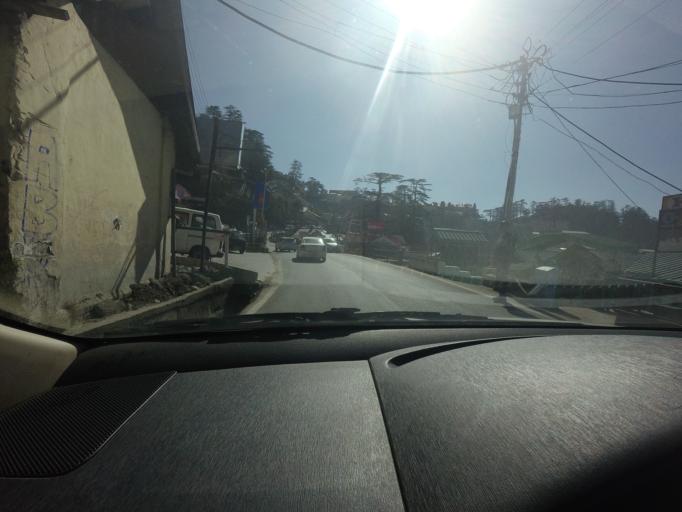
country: IN
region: Himachal Pradesh
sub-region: Shimla
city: Shimla
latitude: 31.1085
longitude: 77.1650
